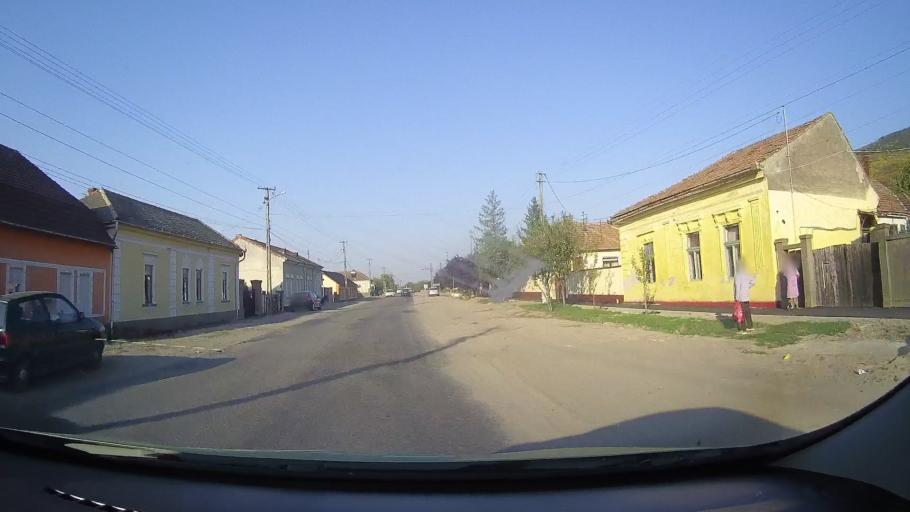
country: RO
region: Arad
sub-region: Comuna Siria
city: Siria
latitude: 46.2725
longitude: 21.6398
